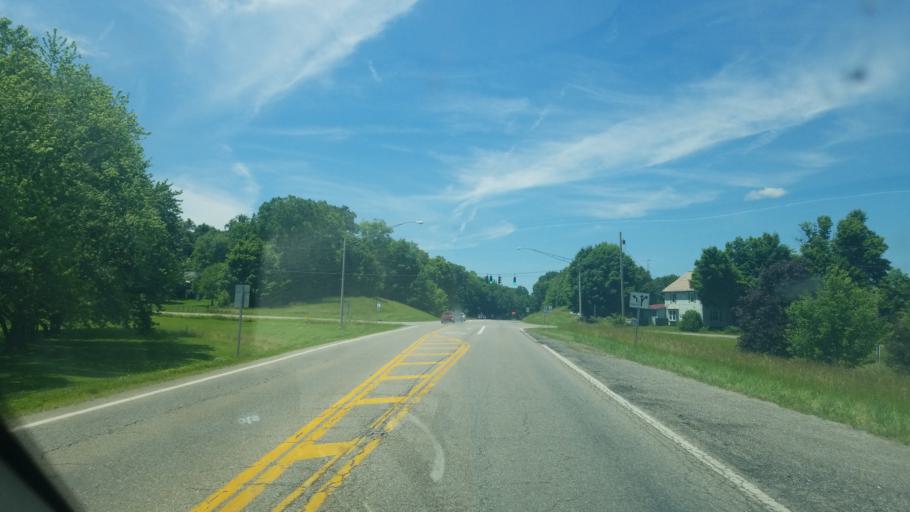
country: US
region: Ohio
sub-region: Columbiana County
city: Salem
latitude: 40.8847
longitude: -80.8741
